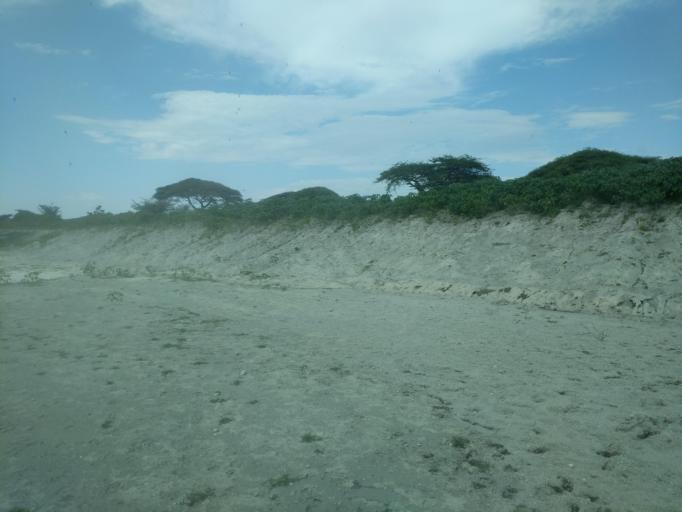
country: ET
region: Oromiya
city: Ziway
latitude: 7.6891
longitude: 38.6465
